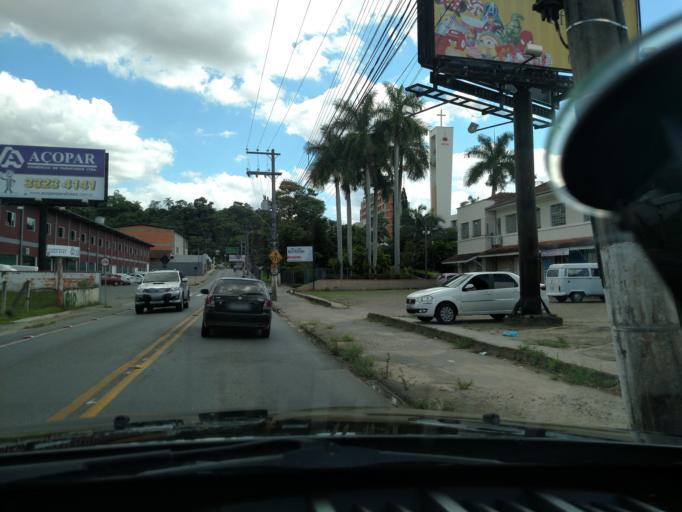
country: BR
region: Santa Catarina
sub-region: Blumenau
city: Blumenau
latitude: -26.8882
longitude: -49.0854
